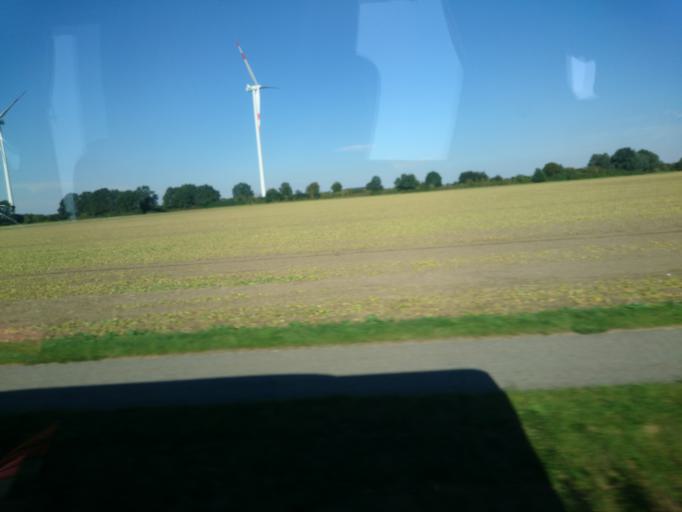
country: DE
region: Mecklenburg-Vorpommern
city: Ducherow
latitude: 53.7731
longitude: 13.7689
